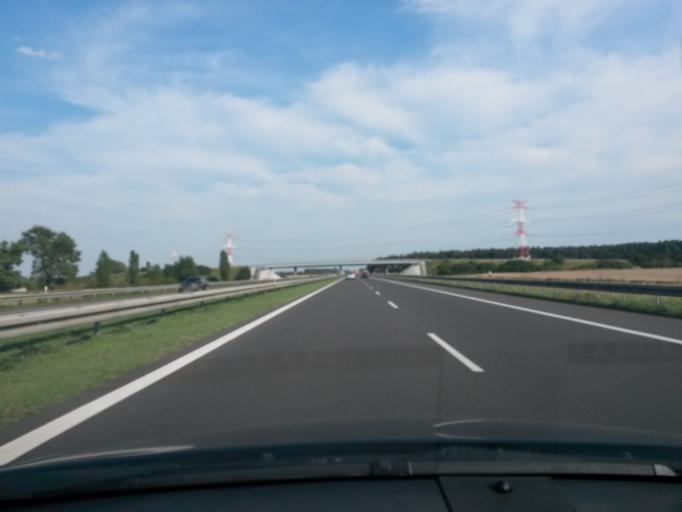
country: PL
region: Greater Poland Voivodeship
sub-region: Powiat wrzesinski
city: Kolaczkowo
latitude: 52.2837
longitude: 17.6852
